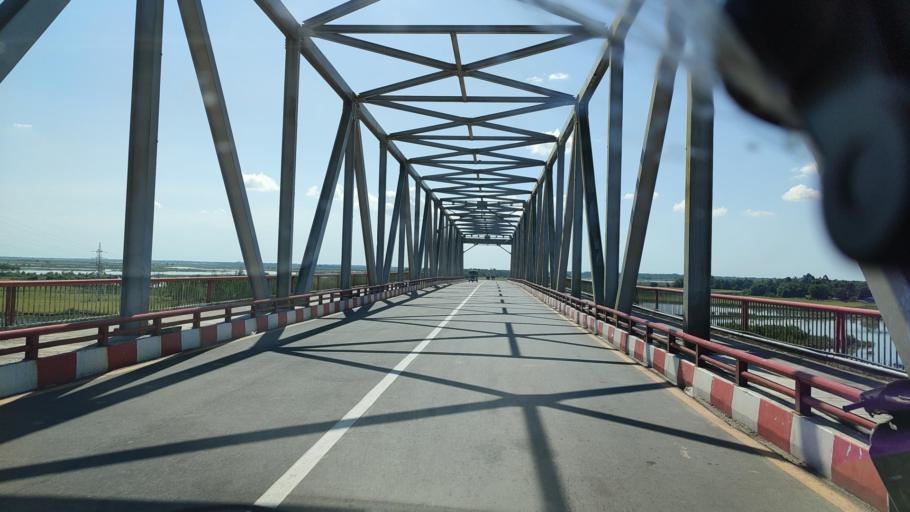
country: MM
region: Rakhine
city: Sittwe
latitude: 20.2984
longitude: 92.8930
